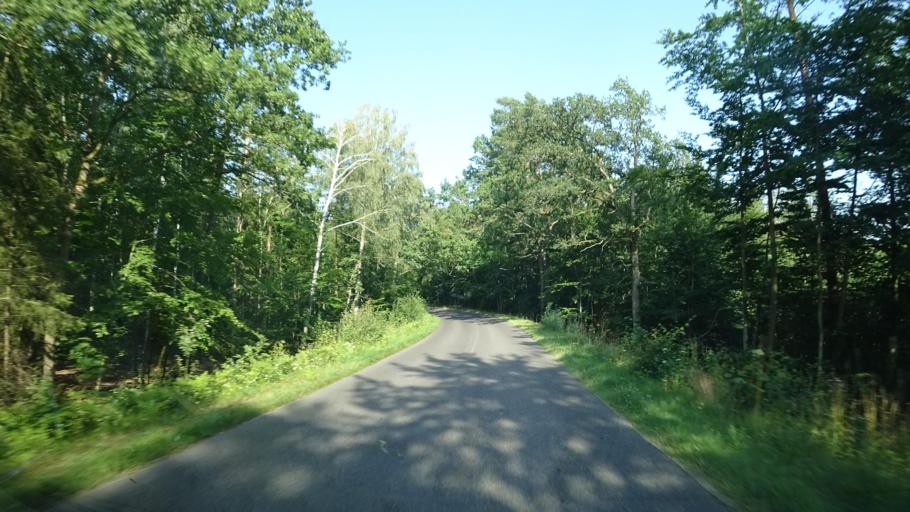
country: PL
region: Pomeranian Voivodeship
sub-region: Powiat czluchowski
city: Przechlewo
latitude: 53.7876
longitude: 17.2085
